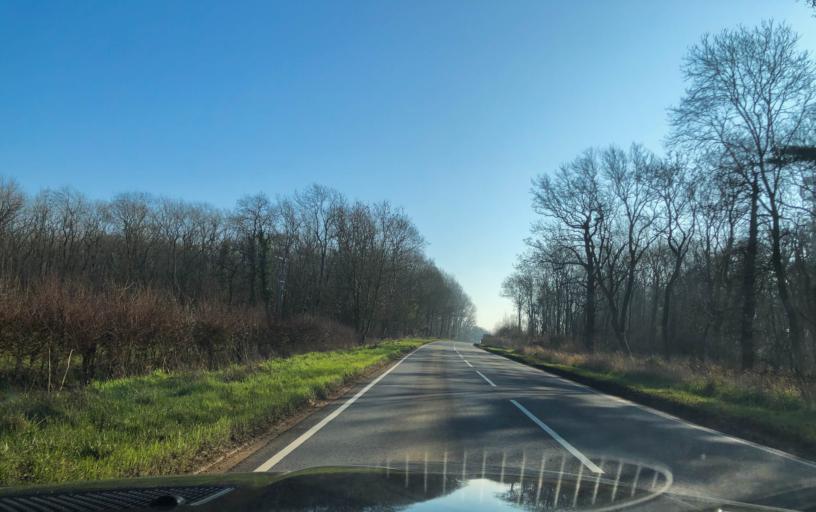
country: GB
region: England
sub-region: Warwickshire
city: Wellesbourne Mountford
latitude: 52.1763
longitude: -1.5619
